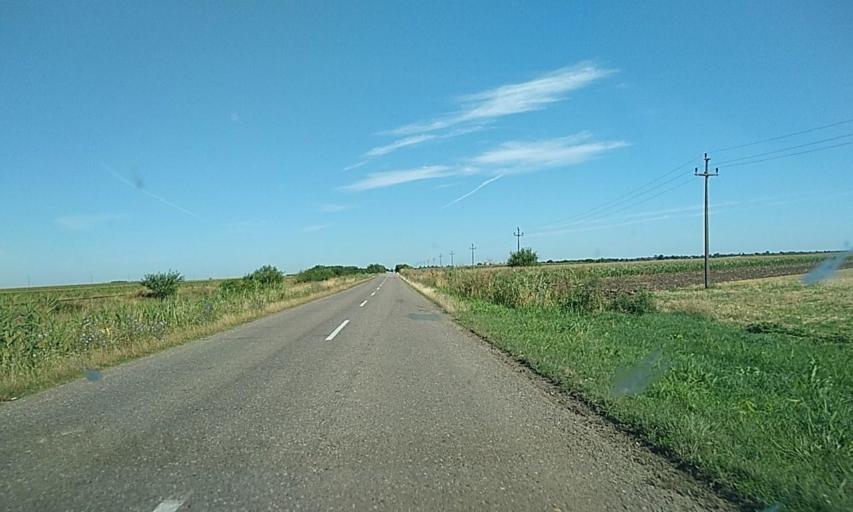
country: RS
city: Backo Gradiste
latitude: 45.4986
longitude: 20.0319
